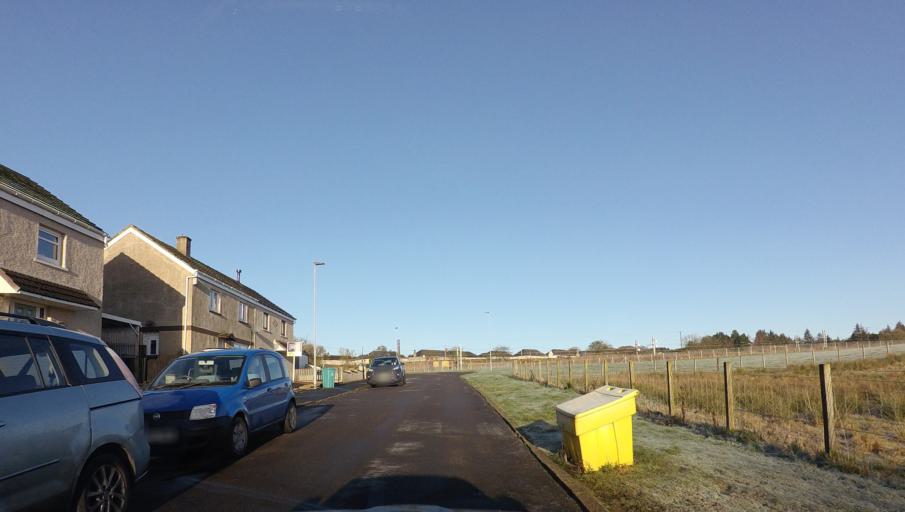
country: GB
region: Scotland
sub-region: North Lanarkshire
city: Shotts
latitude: 55.8107
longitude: -3.8360
